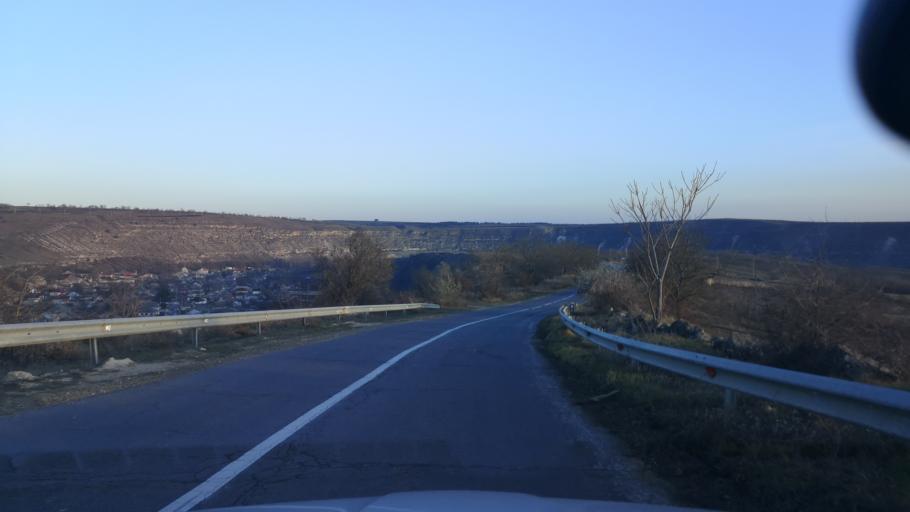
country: MD
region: Telenesti
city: Cocieri
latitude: 47.3105
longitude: 28.9707
